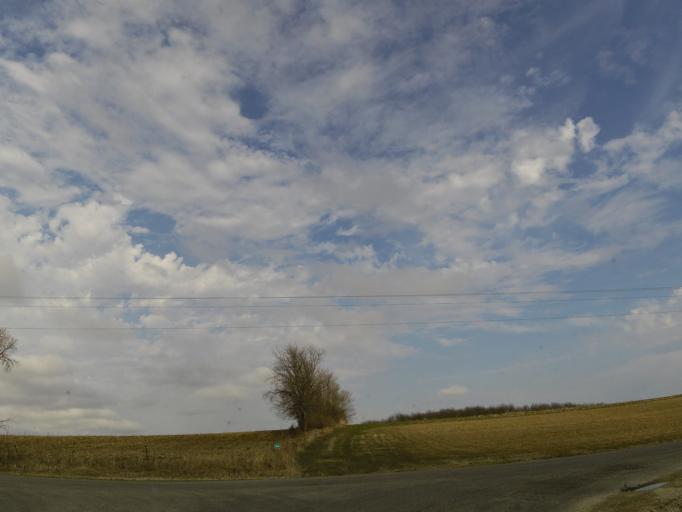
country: US
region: Wisconsin
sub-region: Pierce County
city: Ellsworth
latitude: 44.7504
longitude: -92.4670
